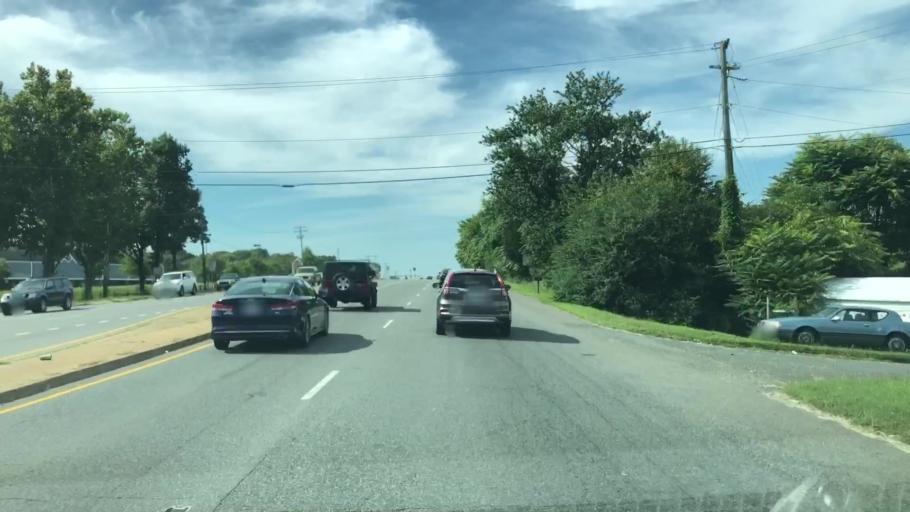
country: US
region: Virginia
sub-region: City of Fredericksburg
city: Fredericksburg
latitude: 38.3003
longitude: -77.4472
